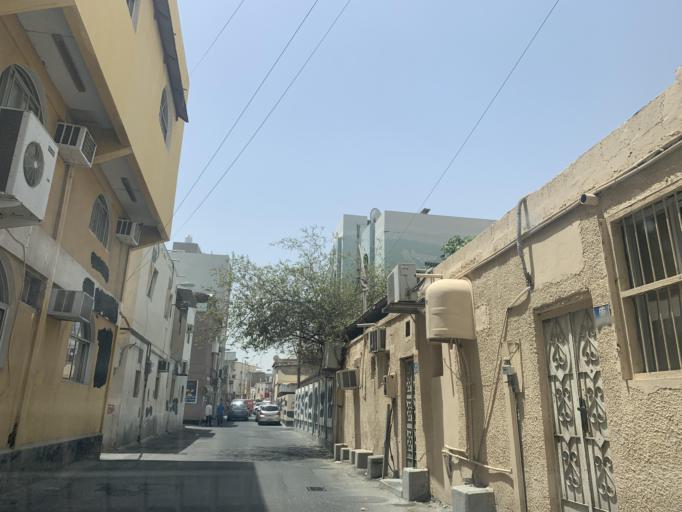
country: BH
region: Manama
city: Jidd Hafs
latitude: 26.2063
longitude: 50.5511
